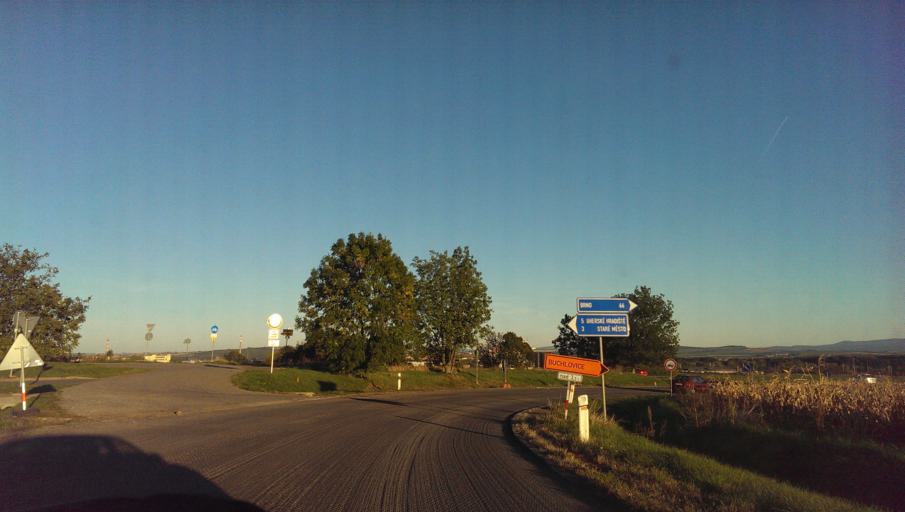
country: CZ
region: Zlin
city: Zlechov
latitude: 49.0741
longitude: 17.3997
